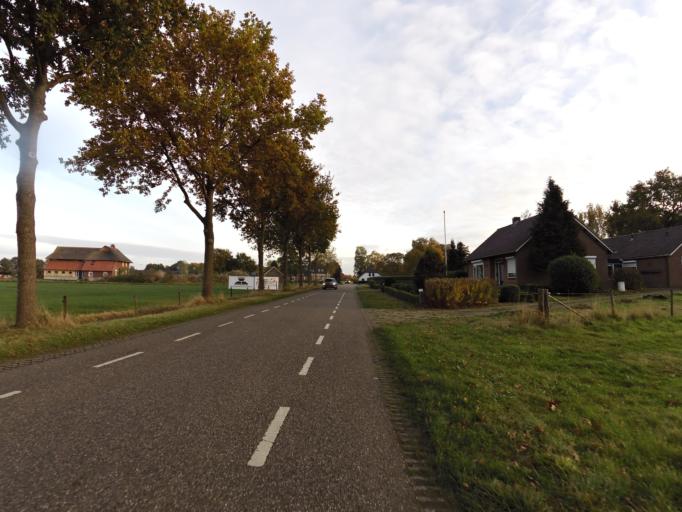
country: NL
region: Gelderland
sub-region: Gemeente Doesburg
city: Doesburg
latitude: 51.9691
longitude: 6.1950
